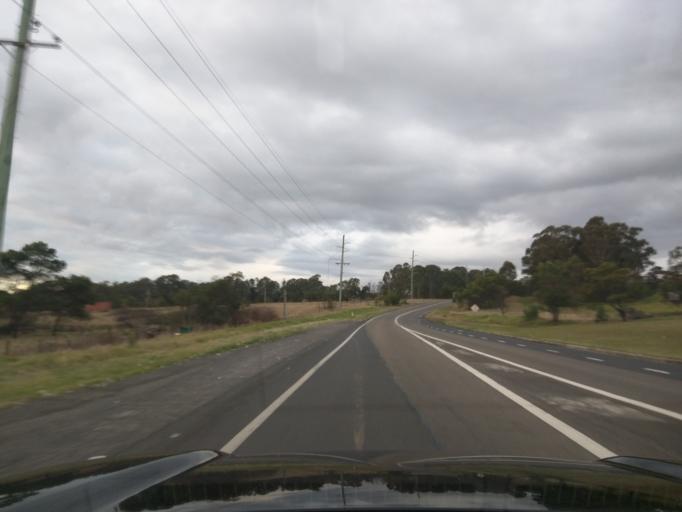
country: AU
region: New South Wales
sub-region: Wollondilly
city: Douglas Park
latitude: -34.2105
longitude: 150.7790
